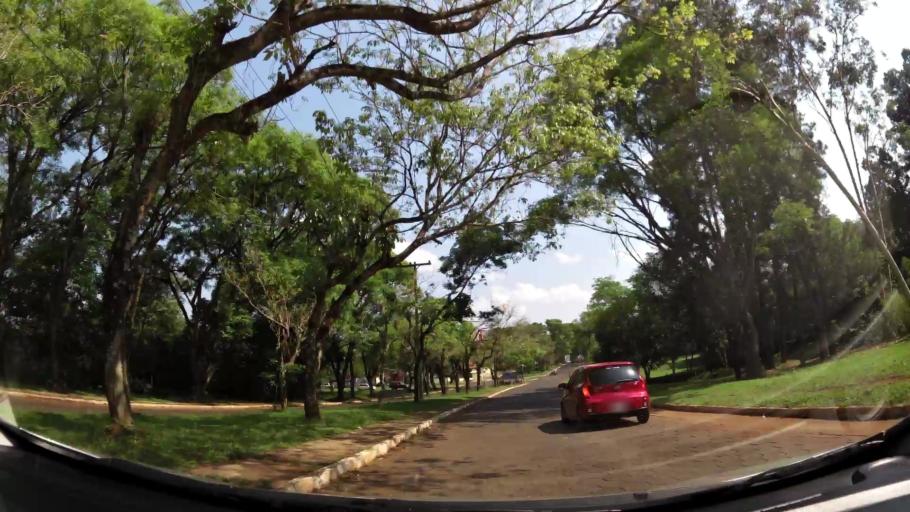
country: PY
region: Alto Parana
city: Ciudad del Este
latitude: -25.5148
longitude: -54.6307
